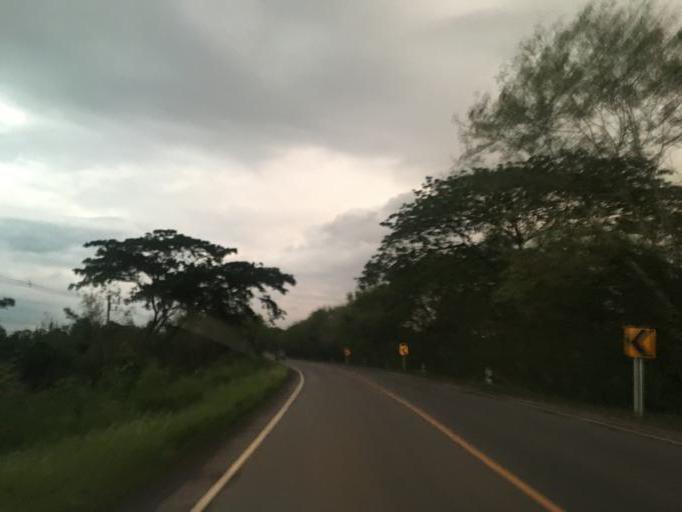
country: TH
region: Changwat Udon Thani
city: Udon Thani
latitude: 17.3137
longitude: 102.7113
